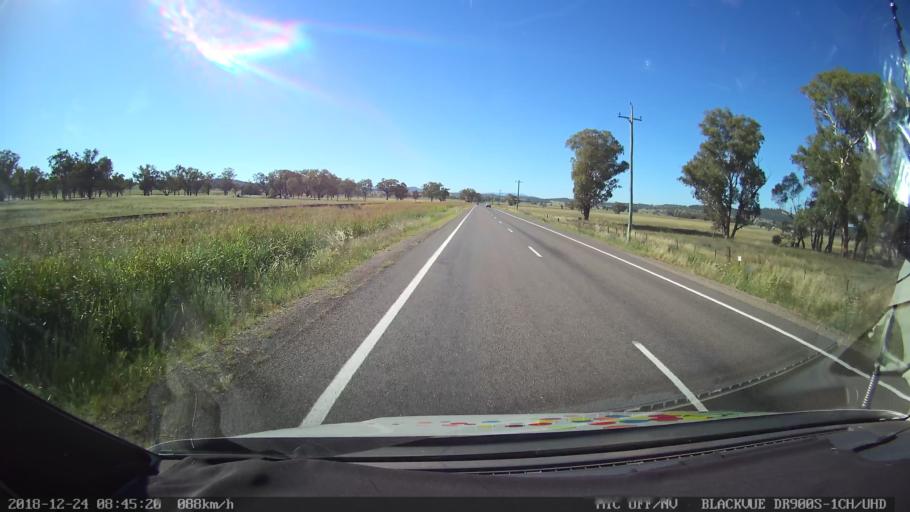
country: AU
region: New South Wales
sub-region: Liverpool Plains
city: Quirindi
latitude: -31.4136
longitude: 150.6516
